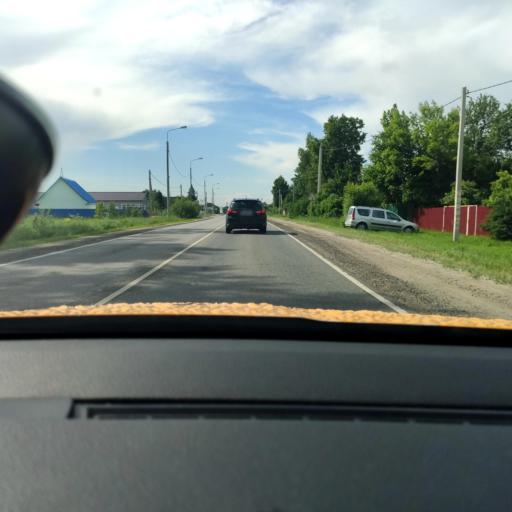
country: RU
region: Moskovskaya
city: Stupino
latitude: 54.9428
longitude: 38.0315
